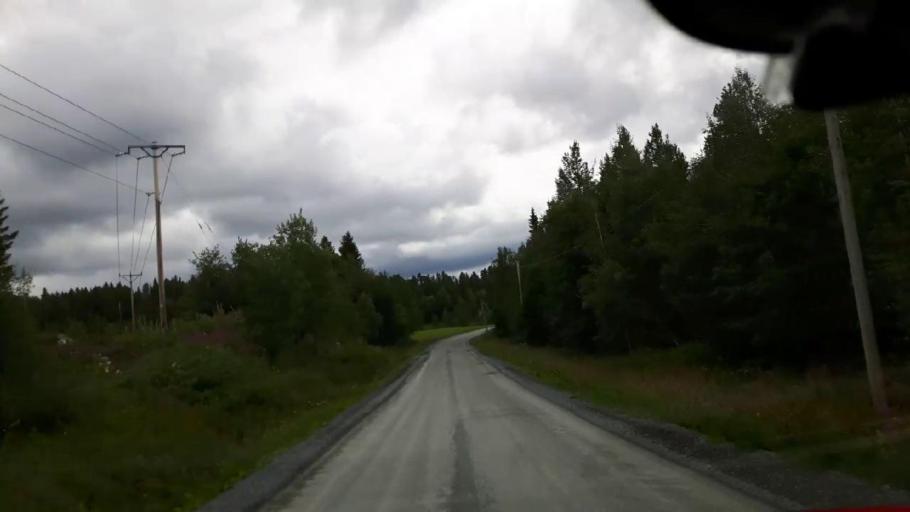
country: SE
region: Jaemtland
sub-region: Krokoms Kommun
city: Krokom
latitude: 63.5737
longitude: 14.2387
